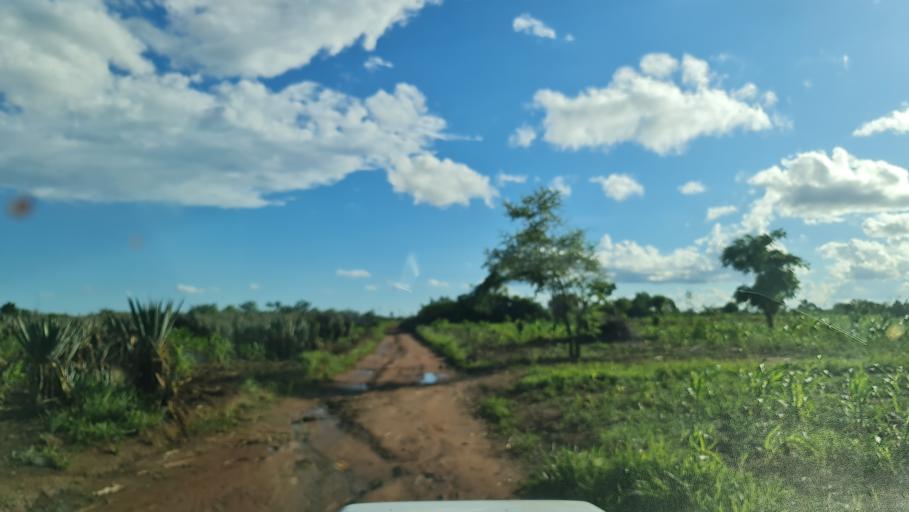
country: MZ
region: Nampula
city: Ilha de Mocambique
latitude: -14.9402
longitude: 40.2001
